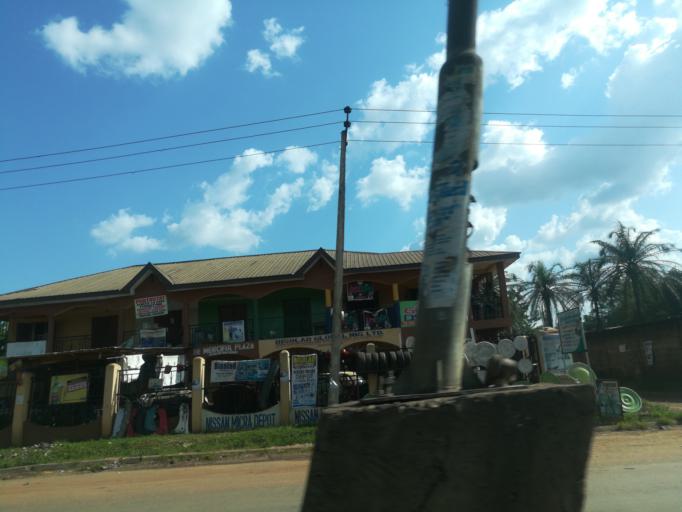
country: NG
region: Oyo
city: Egbeda
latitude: 7.4249
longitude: 3.9880
